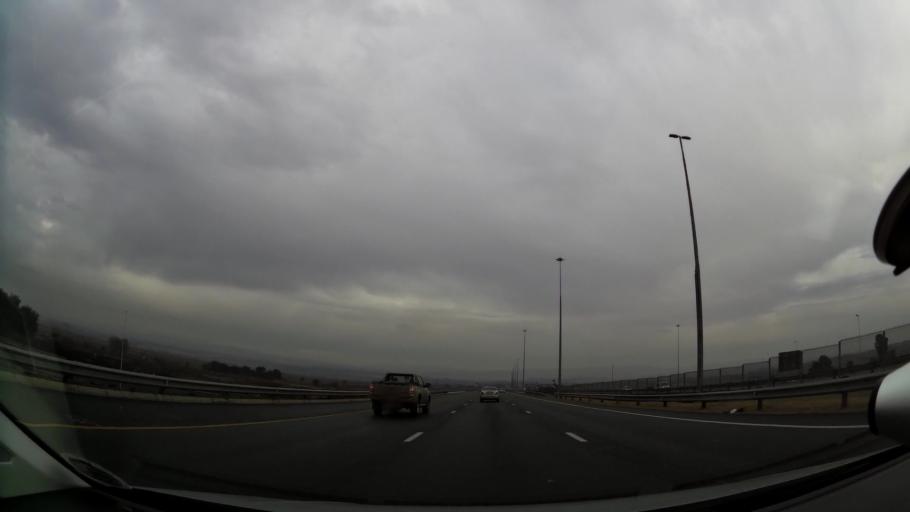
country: ZA
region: Gauteng
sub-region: City of Johannesburg Metropolitan Municipality
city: Soweto
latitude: -26.3037
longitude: 27.9454
